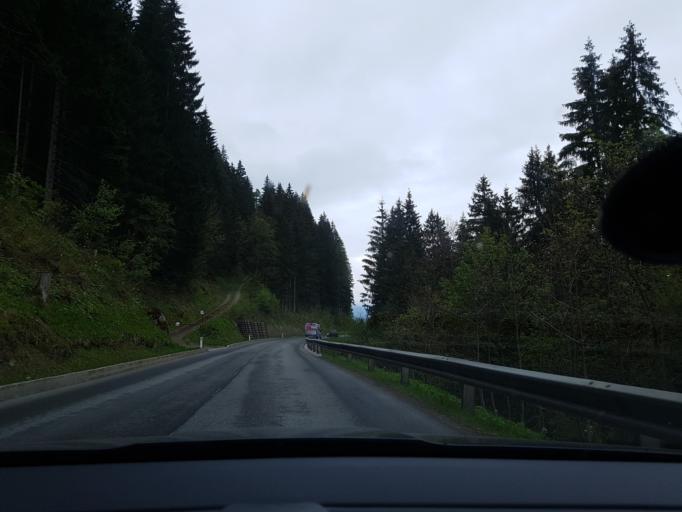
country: AT
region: Tyrol
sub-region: Politischer Bezirk Schwaz
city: Gerlosberg
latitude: 47.2104
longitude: 11.9519
